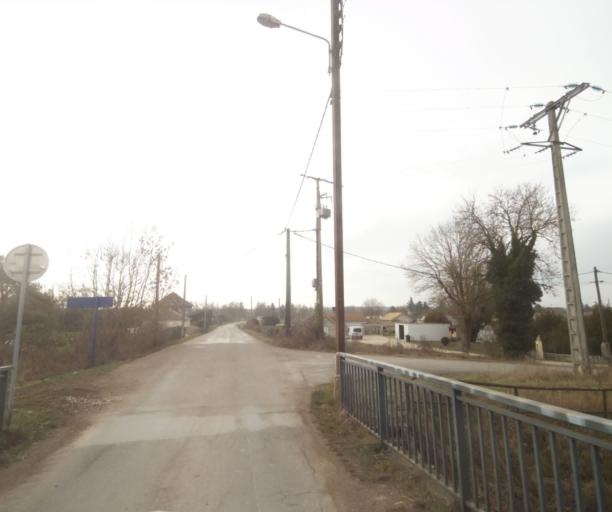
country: FR
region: Champagne-Ardenne
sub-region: Departement de la Haute-Marne
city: Villiers-en-Lieu
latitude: 48.6529
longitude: 4.8208
